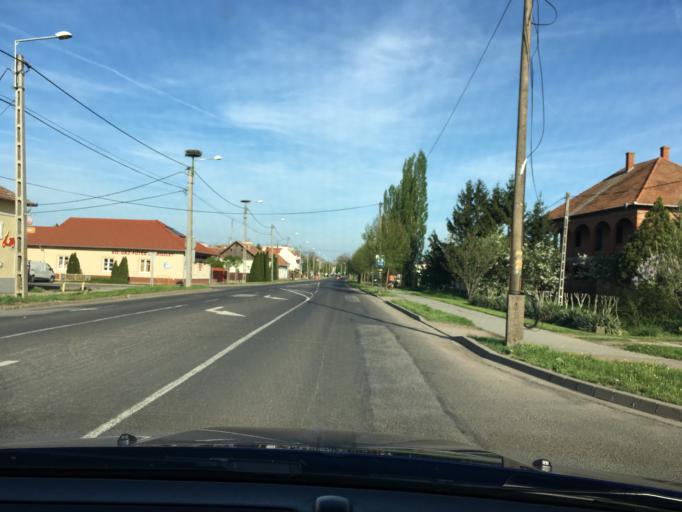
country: HU
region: Bekes
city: Szeghalom
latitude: 47.0160
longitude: 21.1677
